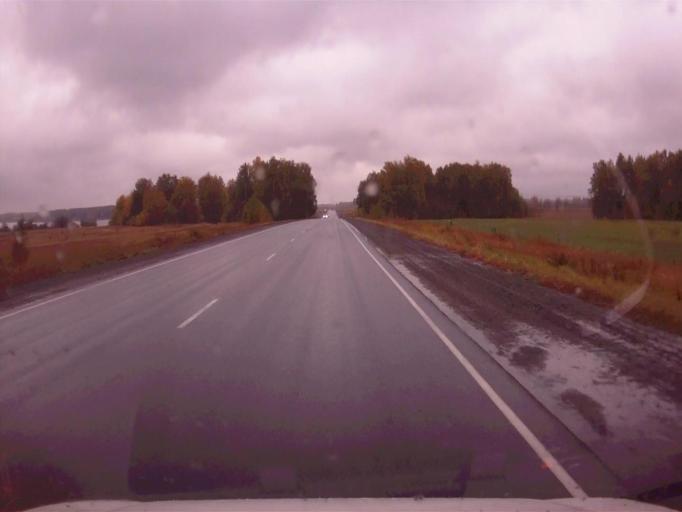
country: RU
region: Chelyabinsk
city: Roshchino
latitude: 55.3862
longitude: 61.1312
